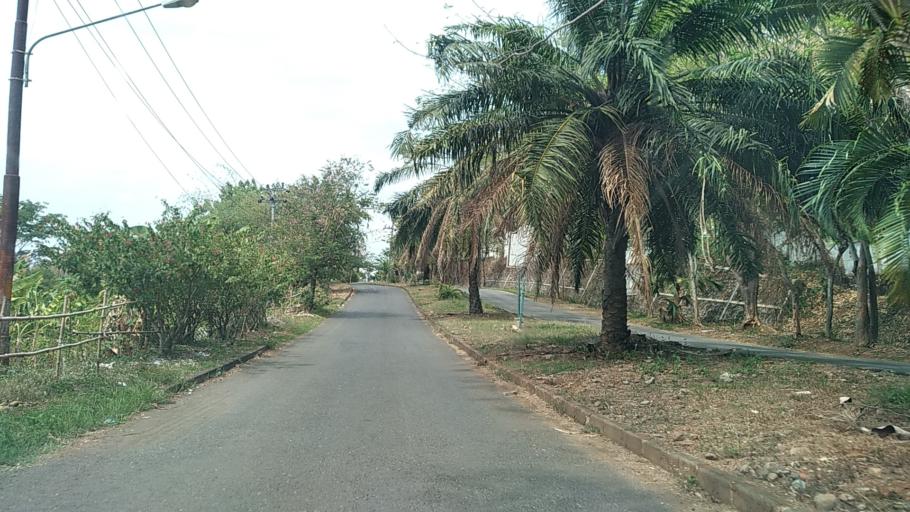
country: ID
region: Central Java
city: Semarang
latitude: -7.0480
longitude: 110.4368
